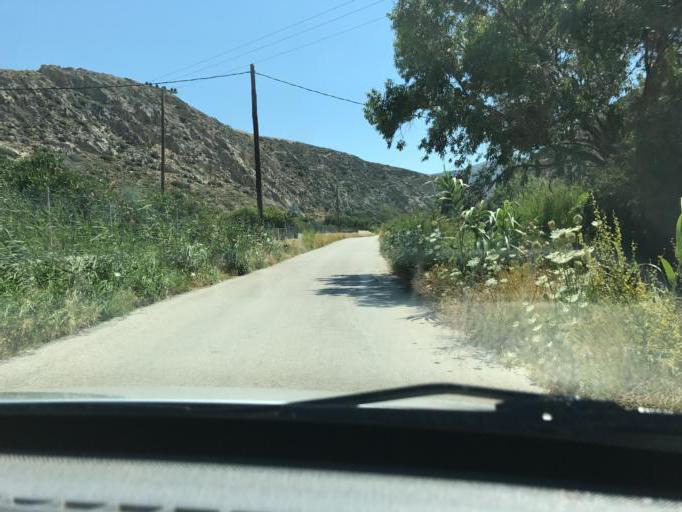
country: GR
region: South Aegean
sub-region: Nomos Dodekanisou
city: Karpathos
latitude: 35.5037
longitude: 27.2016
